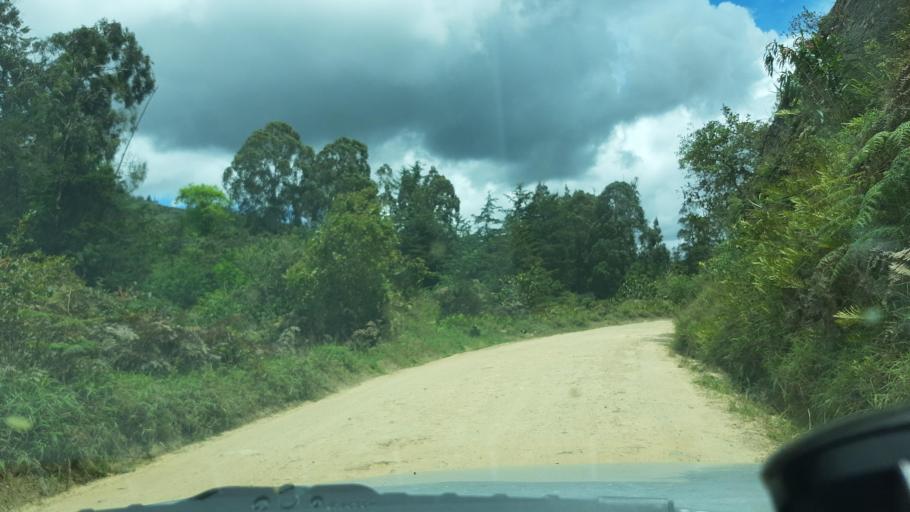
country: CO
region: Cundinamarca
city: Umbita
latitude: 5.2218
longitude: -73.4211
